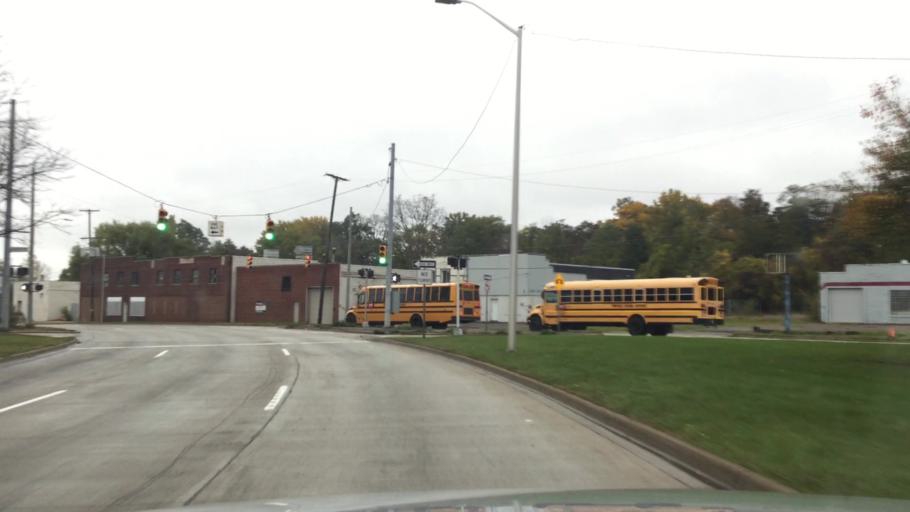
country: US
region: Michigan
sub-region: Oakland County
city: Pontiac
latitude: 42.6411
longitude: -83.2984
